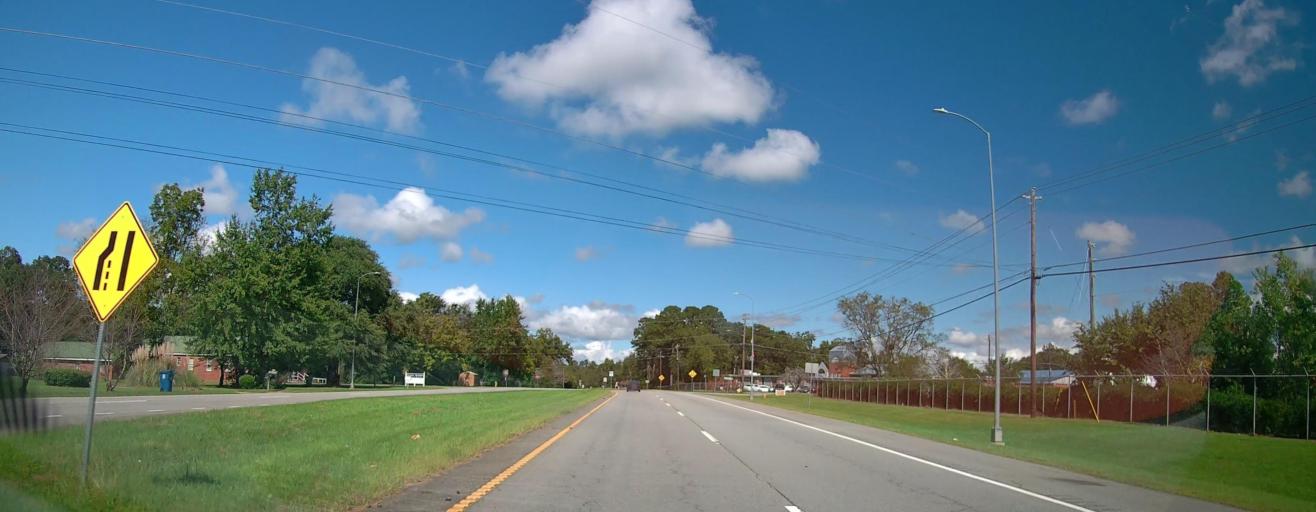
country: US
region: Georgia
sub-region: Bibb County
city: Macon
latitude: 32.8122
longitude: -83.5689
